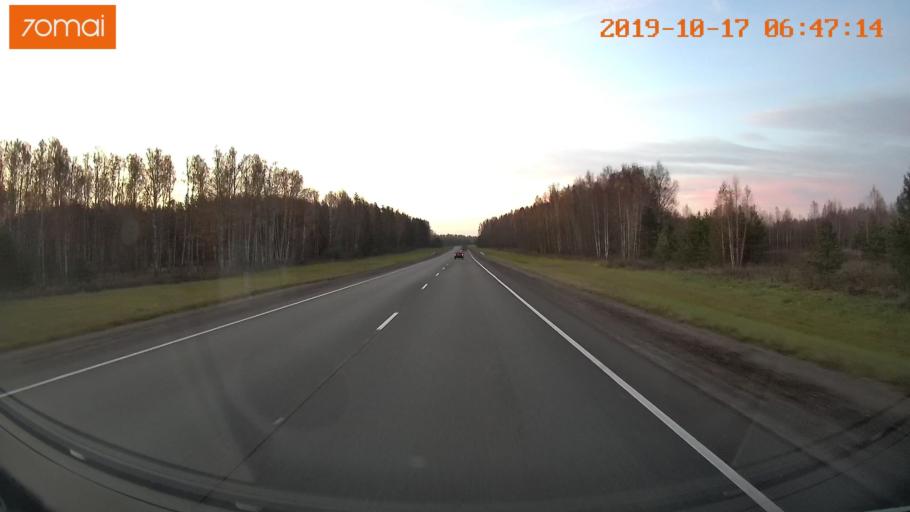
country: RU
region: Vladimir
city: Kideksha
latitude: 56.5390
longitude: 40.5559
